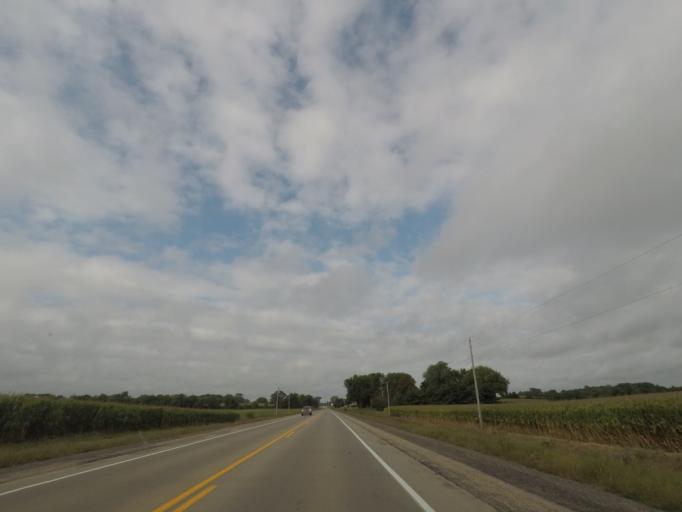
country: US
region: Wisconsin
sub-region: Dane County
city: Deerfield
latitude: 43.0321
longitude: -89.1405
